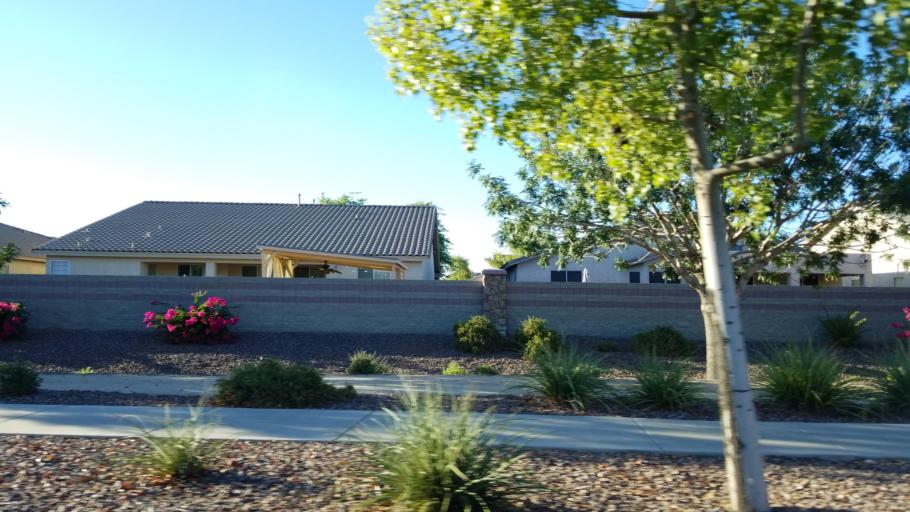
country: US
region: Arizona
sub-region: Maricopa County
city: Laveen
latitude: 33.3775
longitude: -112.2120
